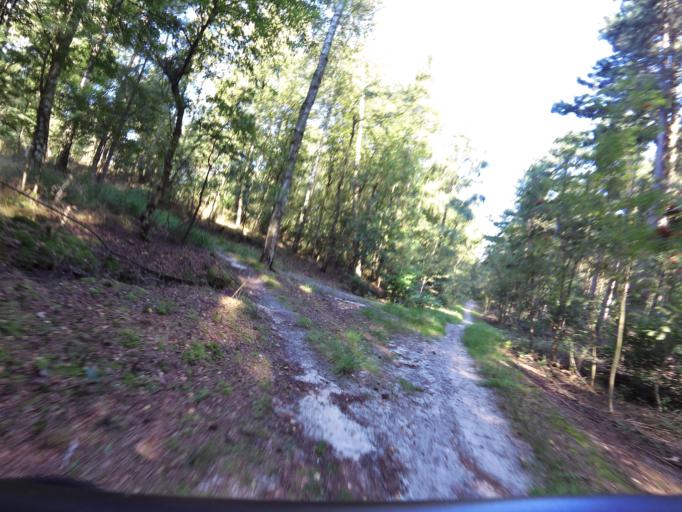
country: BE
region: Flanders
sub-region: Provincie Antwerpen
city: Stabroek
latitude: 51.3649
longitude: 4.3480
